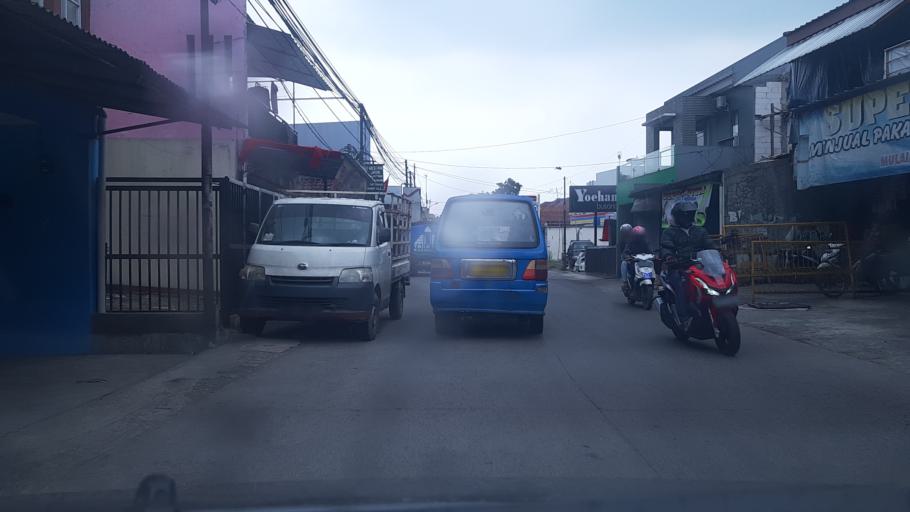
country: ID
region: West Java
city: Bogor
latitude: -6.5659
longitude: 106.8640
